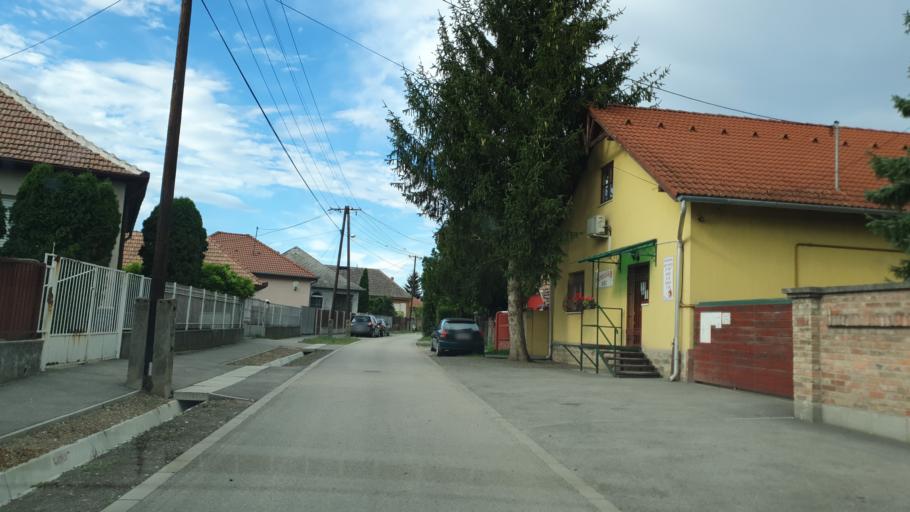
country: HU
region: Heves
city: Lorinci
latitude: 47.7464
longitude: 19.6760
